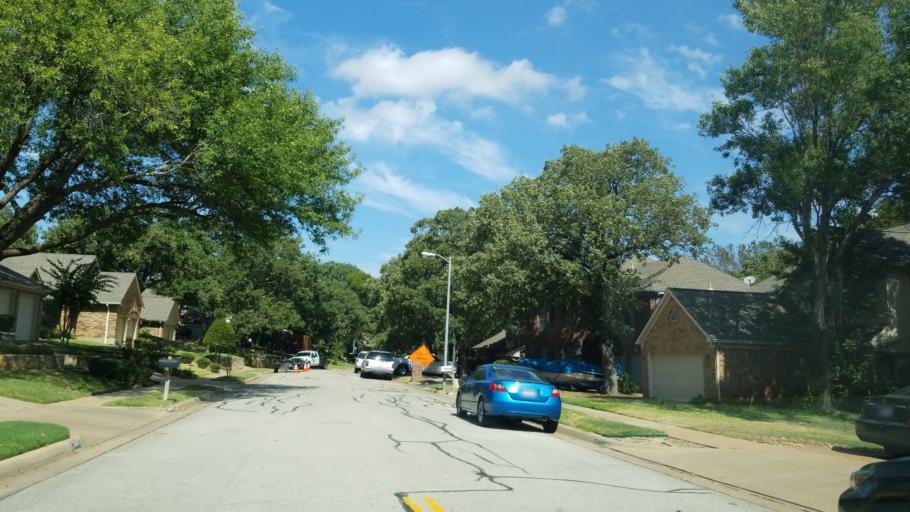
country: US
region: Texas
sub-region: Tarrant County
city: Euless
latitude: 32.8569
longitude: -97.1016
